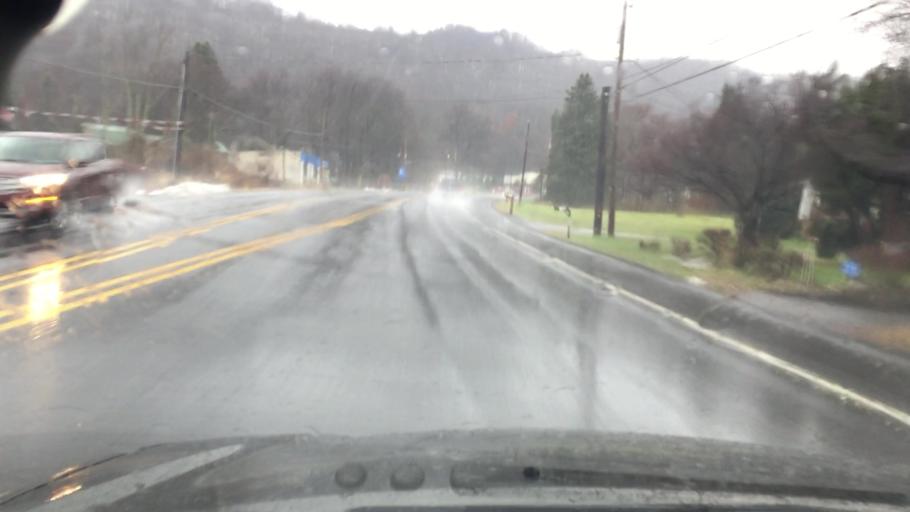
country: US
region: Pennsylvania
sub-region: Luzerne County
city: Harleigh
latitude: 41.0097
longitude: -75.9661
